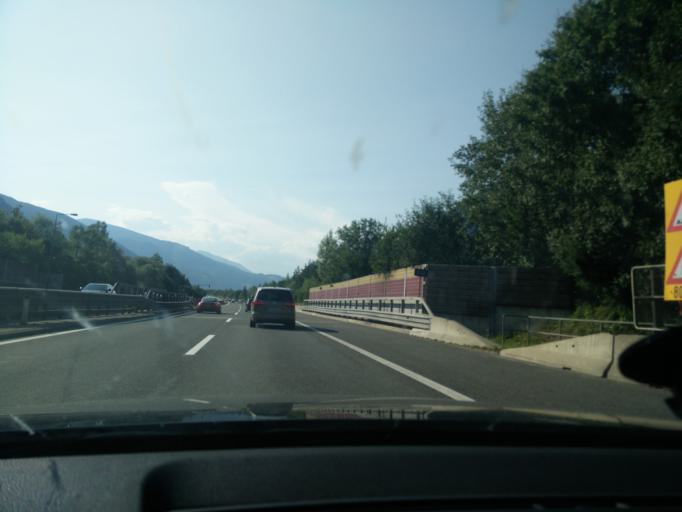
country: AT
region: Carinthia
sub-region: Villach Stadt
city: Villach
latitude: 46.6418
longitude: 13.8871
